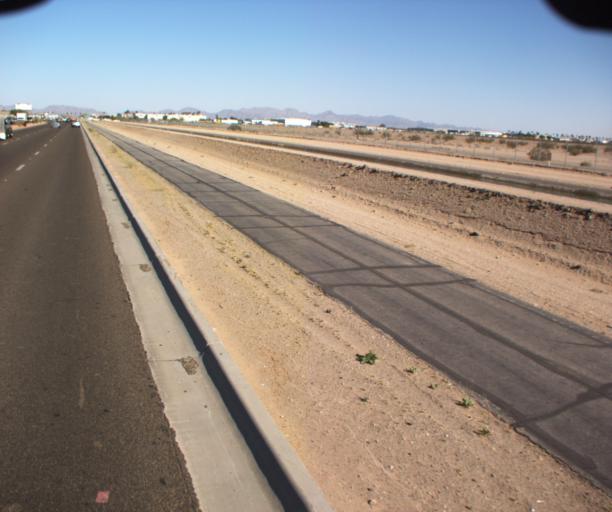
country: US
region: Arizona
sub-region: Yuma County
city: Yuma
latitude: 32.6695
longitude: -114.5878
